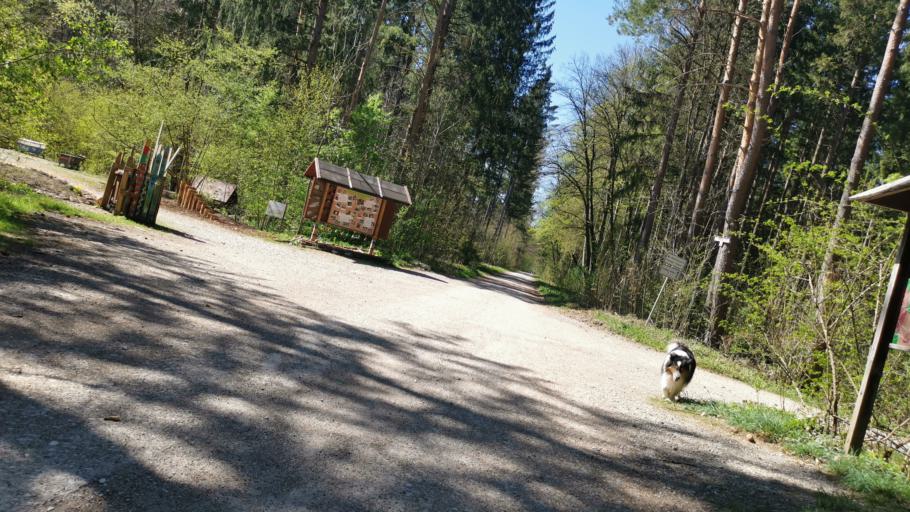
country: DE
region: Bavaria
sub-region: Upper Bavaria
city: Neuried
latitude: 48.0859
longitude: 11.4490
